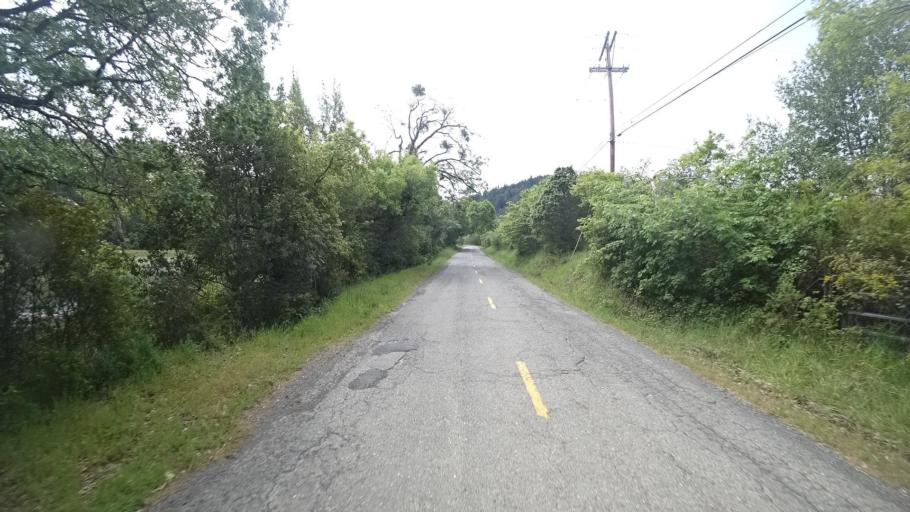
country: US
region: California
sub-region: Humboldt County
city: Redway
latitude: 40.0716
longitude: -123.8284
